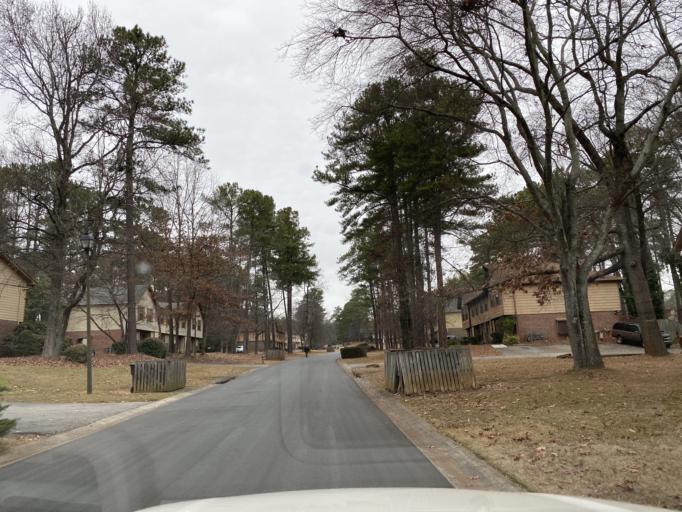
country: US
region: Georgia
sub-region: Cobb County
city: Fair Oaks
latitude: 33.9200
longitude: -84.5710
